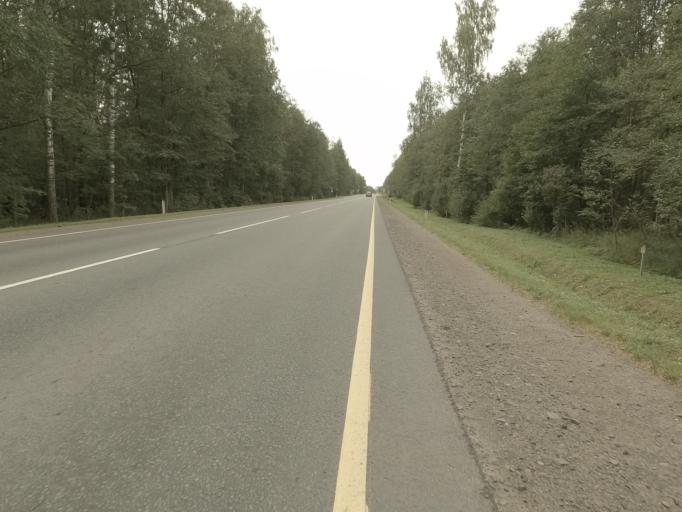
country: RU
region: Leningrad
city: Kirovsk
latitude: 59.8503
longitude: 31.0286
